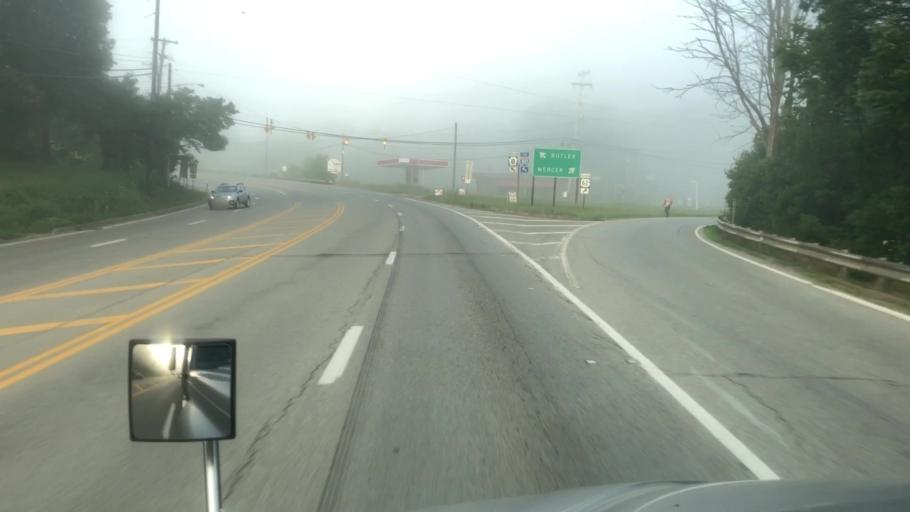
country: US
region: Pennsylvania
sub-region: Venango County
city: Franklin
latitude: 41.3856
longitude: -79.8482
